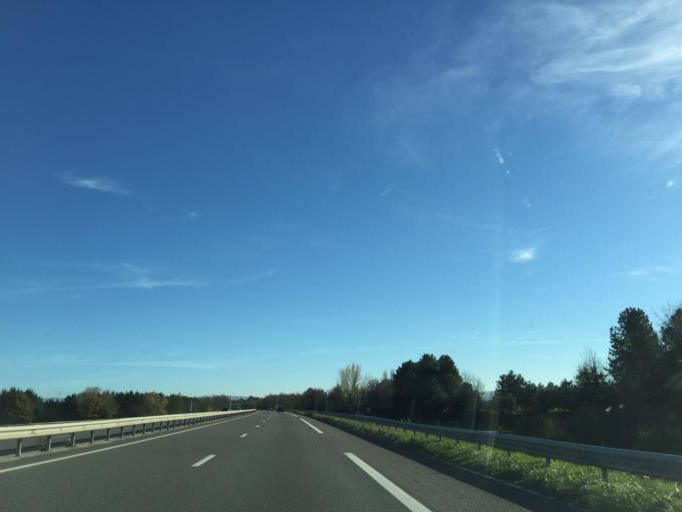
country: FR
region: Rhone-Alpes
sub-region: Departement de la Loire
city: Saint-Cyprien
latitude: 45.5796
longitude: 4.2152
